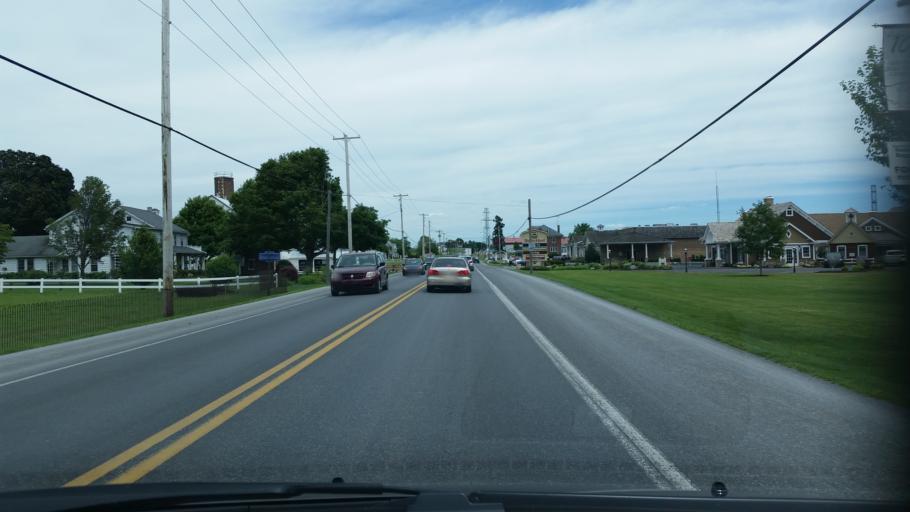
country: US
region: Pennsylvania
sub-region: Lancaster County
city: Paradise
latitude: 40.0385
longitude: -76.1763
